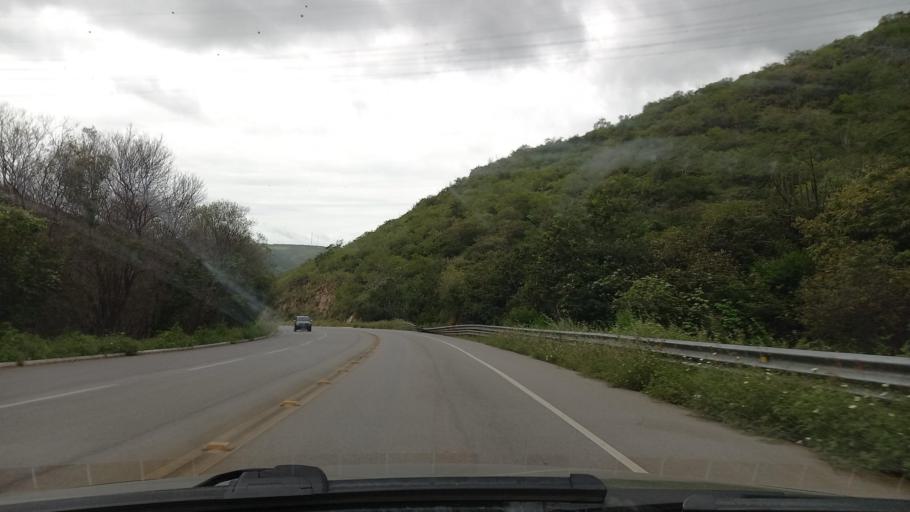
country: BR
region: Sergipe
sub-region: Caninde De Sao Francisco
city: Caninde de Sao Francisco
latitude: -9.6452
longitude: -37.7951
